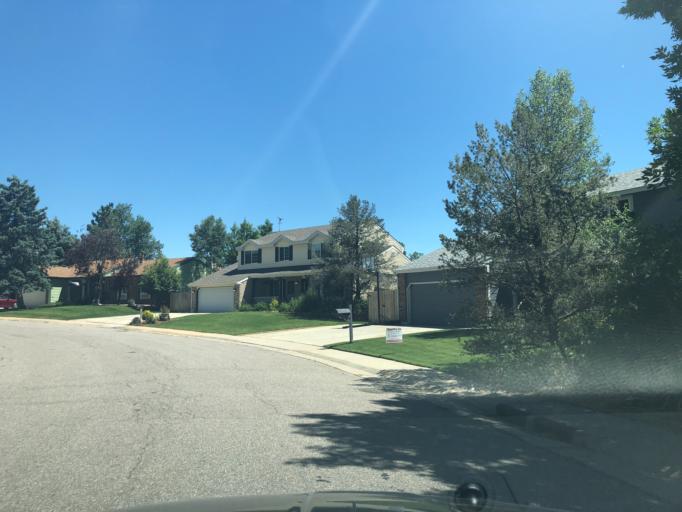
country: US
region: Colorado
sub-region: Arapahoe County
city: Dove Valley
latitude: 39.6163
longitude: -104.7868
